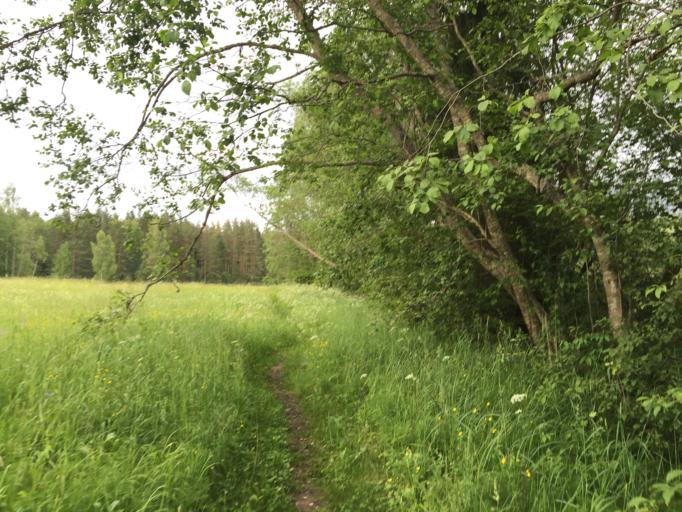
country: LV
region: Ligatne
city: Ligatne
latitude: 57.2389
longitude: 25.1502
